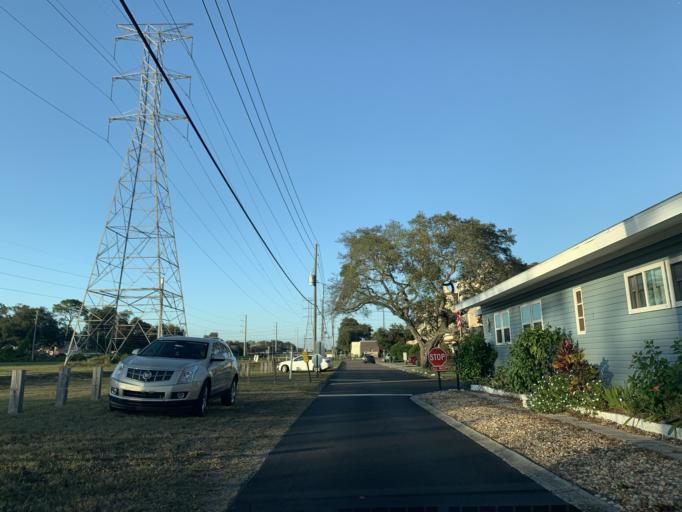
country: US
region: Florida
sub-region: Pinellas County
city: South Highpoint
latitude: 27.9556
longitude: -82.7334
